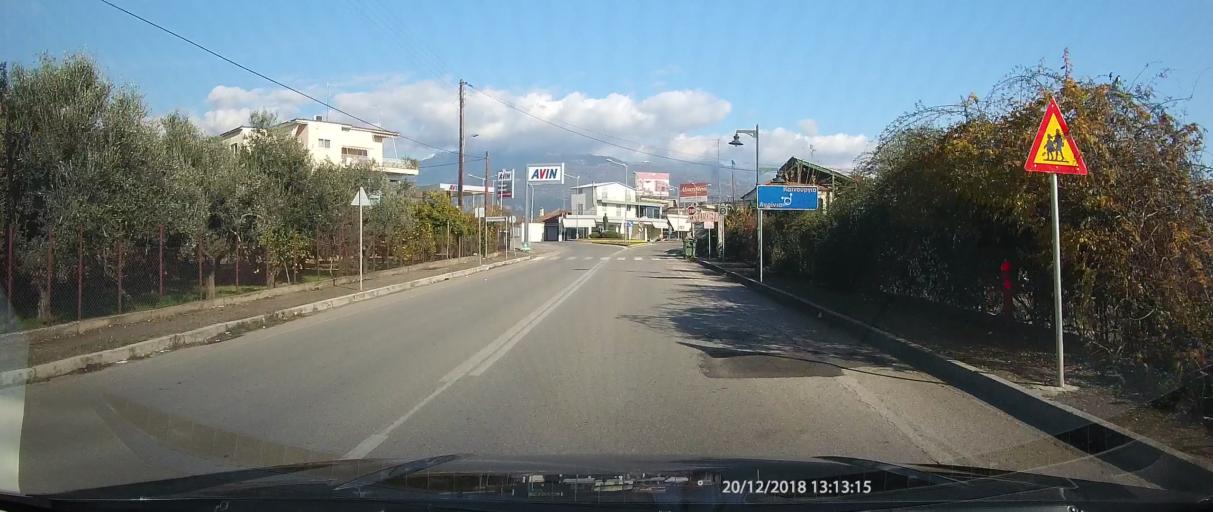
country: GR
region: West Greece
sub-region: Nomos Aitolias kai Akarnanias
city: Kainouryion
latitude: 38.6025
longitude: 21.4777
